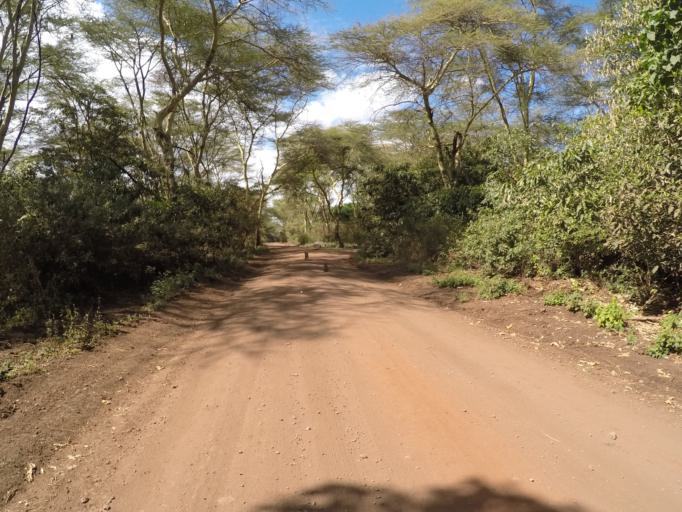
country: TZ
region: Arusha
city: Mto wa Mbu
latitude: -3.4055
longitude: 35.8251
